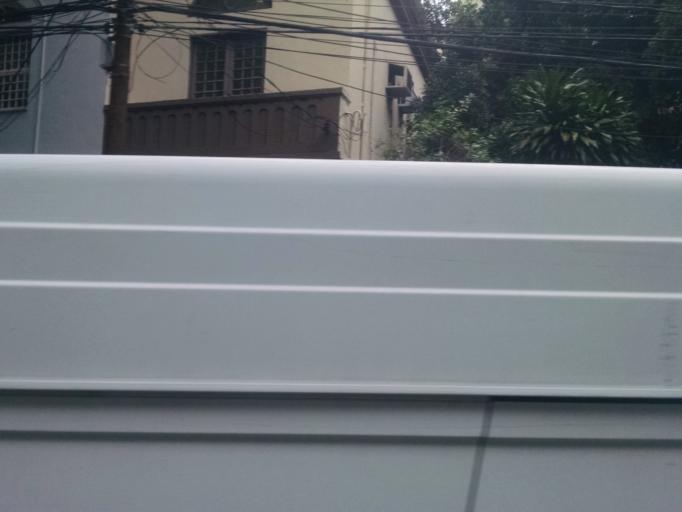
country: BR
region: Rio de Janeiro
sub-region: Rio De Janeiro
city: Rio de Janeiro
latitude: -22.9523
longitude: -43.1960
